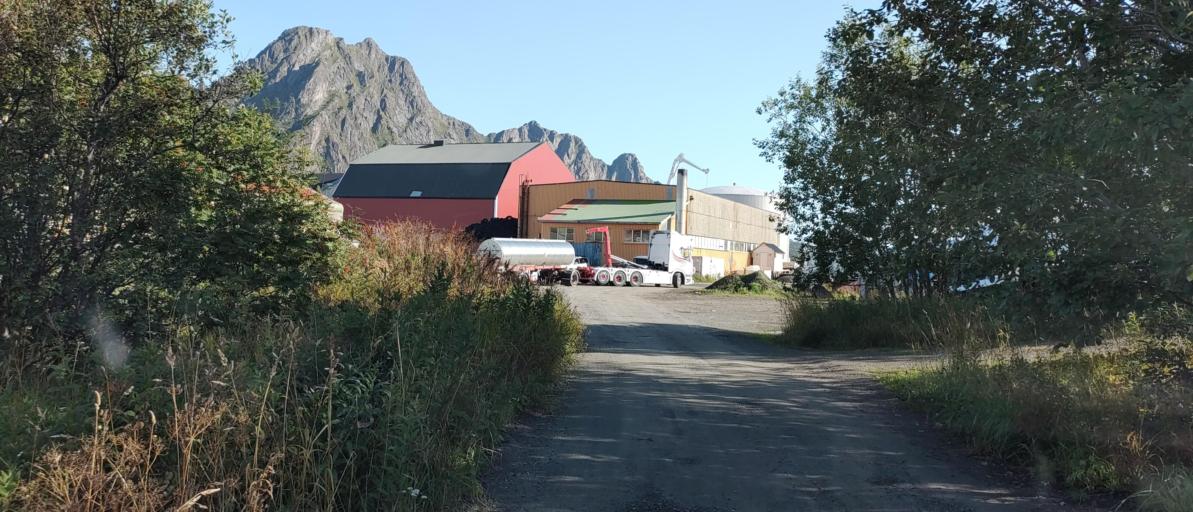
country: NO
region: Nordland
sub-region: Vagan
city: Svolvaer
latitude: 68.2287
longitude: 14.5712
